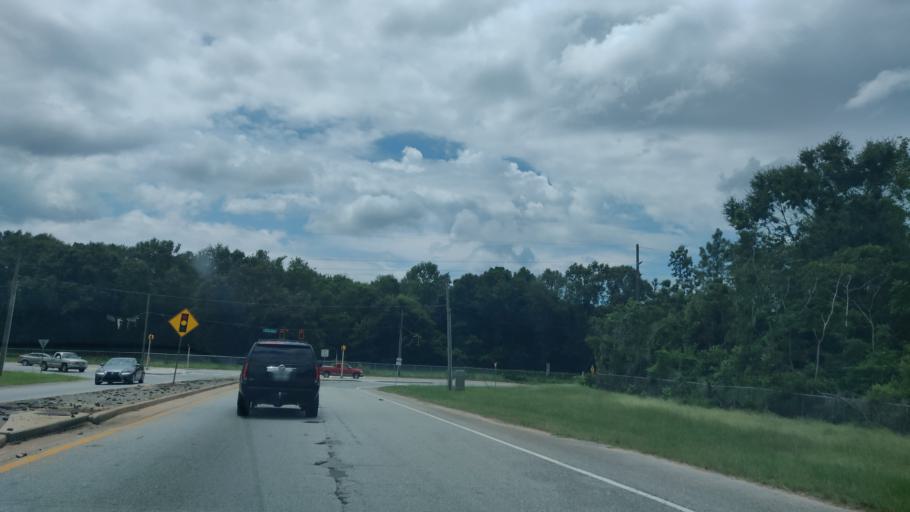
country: US
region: Georgia
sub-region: Dougherty County
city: Albany
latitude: 31.5807
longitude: -84.1140
